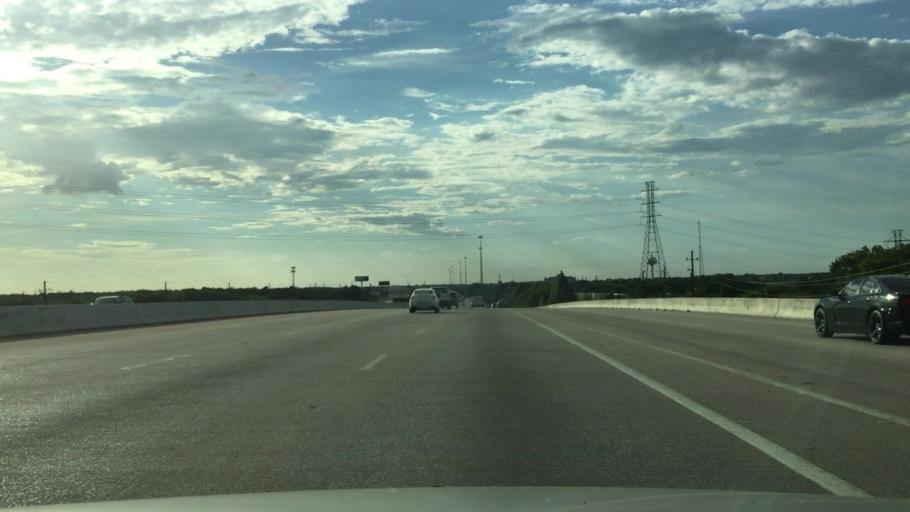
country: US
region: Texas
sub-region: Harris County
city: Hudson
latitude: 29.9450
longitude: -95.5265
